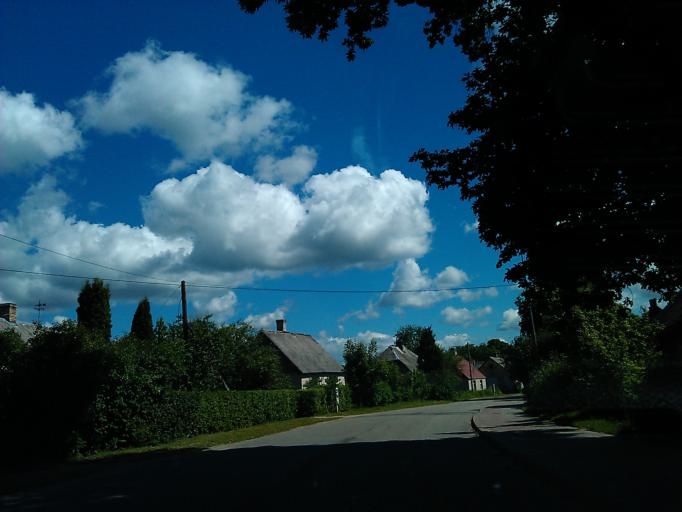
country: LV
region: Varaklani
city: Varaklani
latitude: 56.6074
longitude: 26.7434
